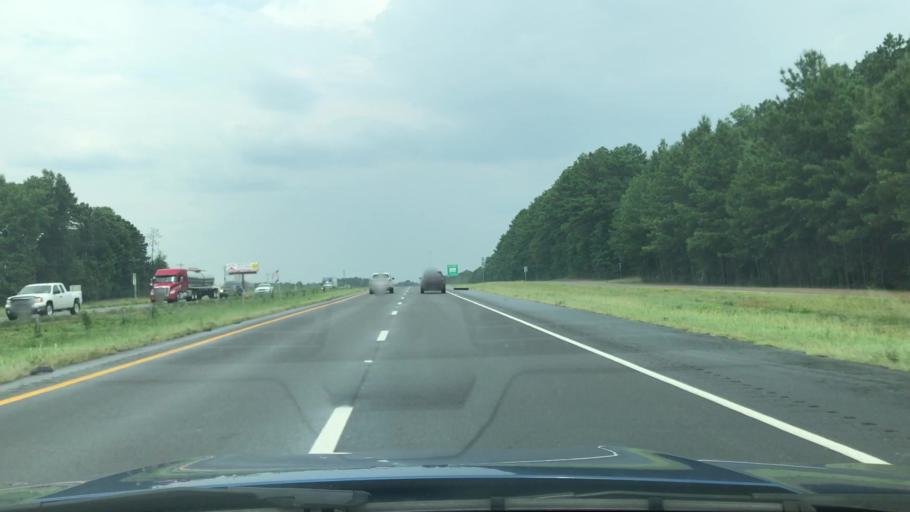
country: US
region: Texas
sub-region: Harrison County
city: Hallsville
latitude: 32.4858
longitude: -94.4838
